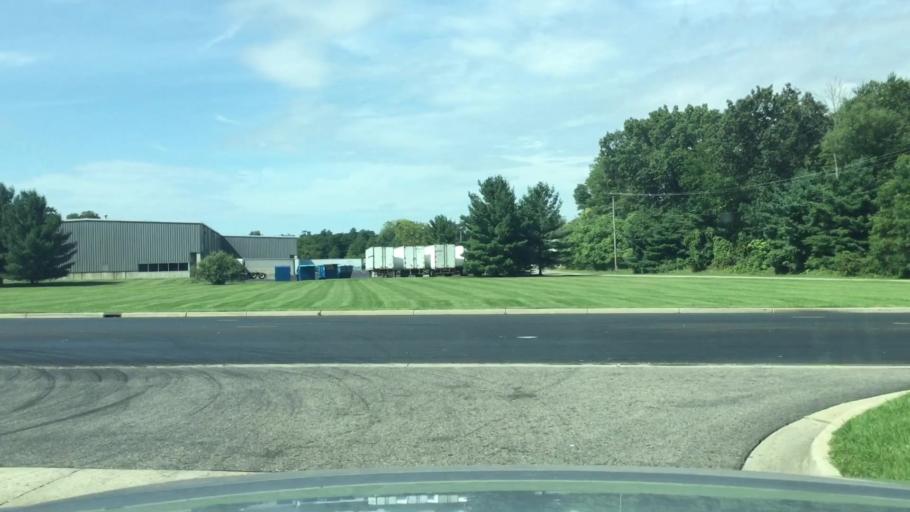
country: US
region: Michigan
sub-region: Kalamazoo County
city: Galesburg
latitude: 42.2762
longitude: -85.4285
